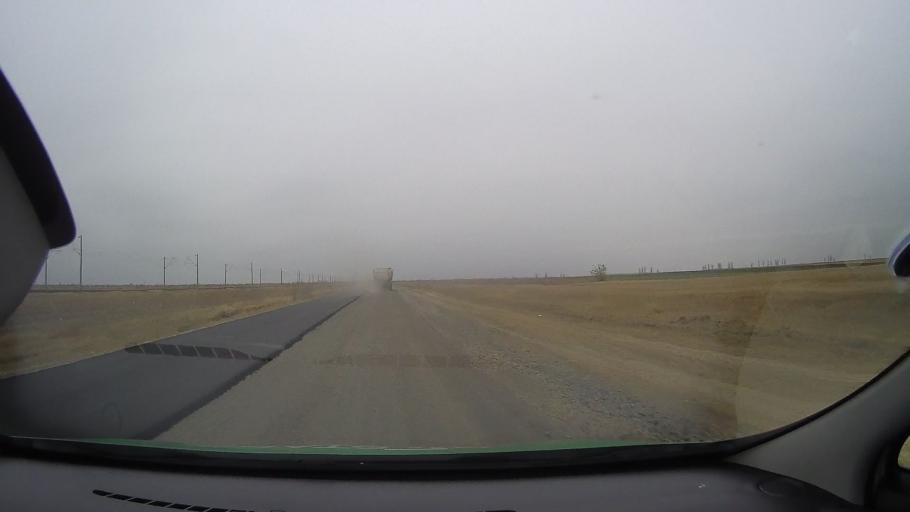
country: RO
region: Braila
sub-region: Comuna Baraganul
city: Baraganul
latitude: 44.7956
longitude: 27.5315
